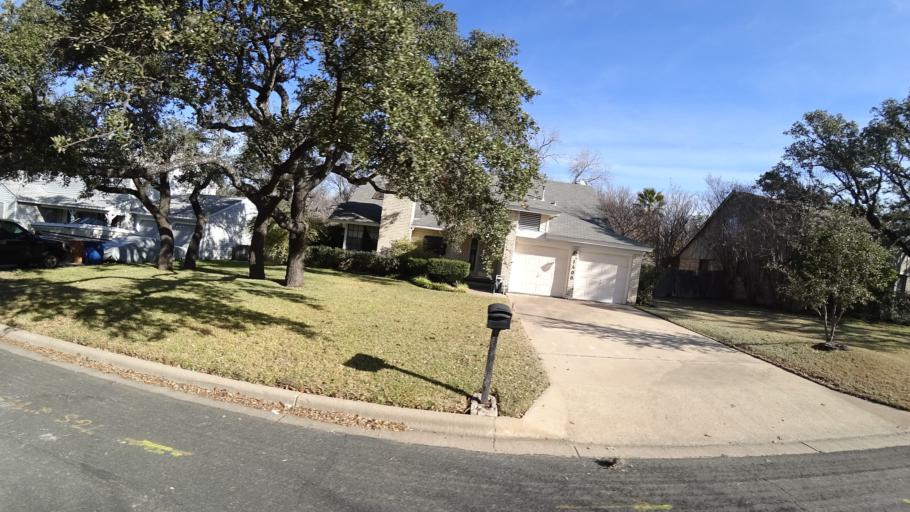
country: US
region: Texas
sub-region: Travis County
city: Wells Branch
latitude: 30.3917
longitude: -97.6938
